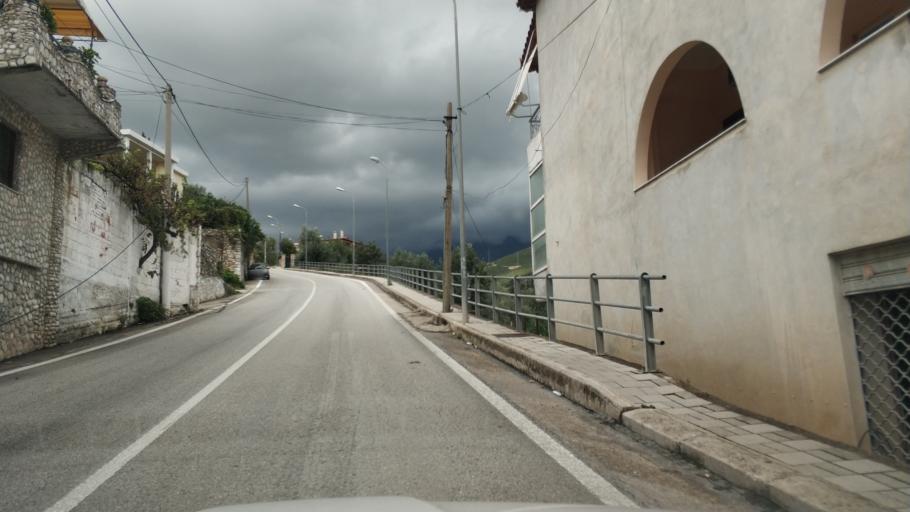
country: AL
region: Vlore
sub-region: Rrethi i Vlores
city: Himare
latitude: 40.1084
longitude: 19.7413
